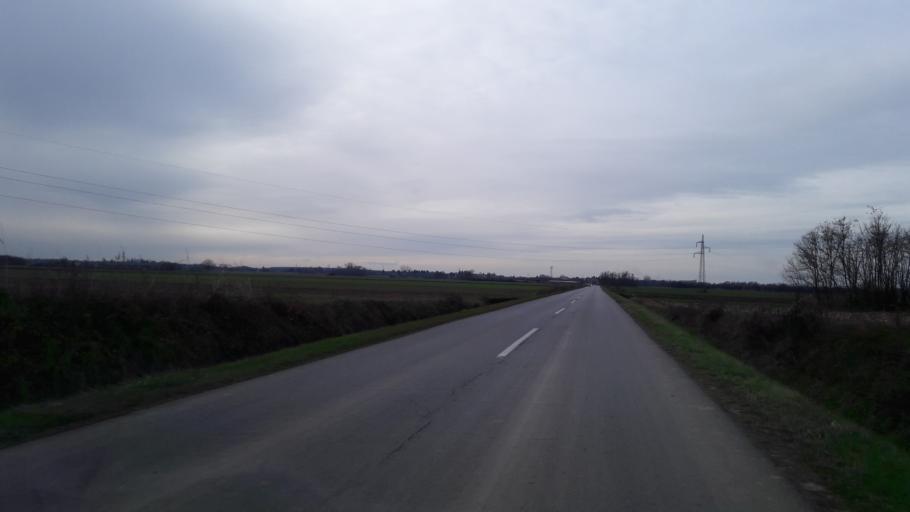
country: HR
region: Osjecko-Baranjska
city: Semeljci
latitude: 45.3764
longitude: 18.5563
